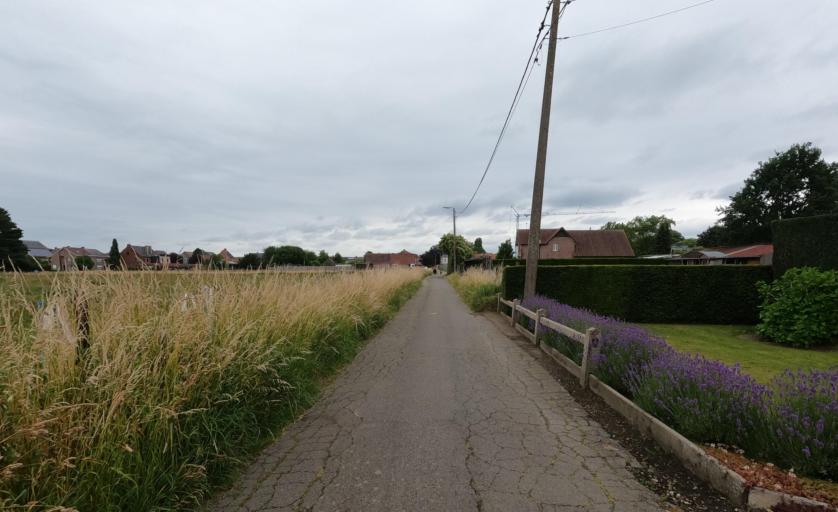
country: BE
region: Flanders
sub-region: Provincie Antwerpen
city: Heist-op-den-Berg
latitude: 51.1008
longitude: 4.7266
